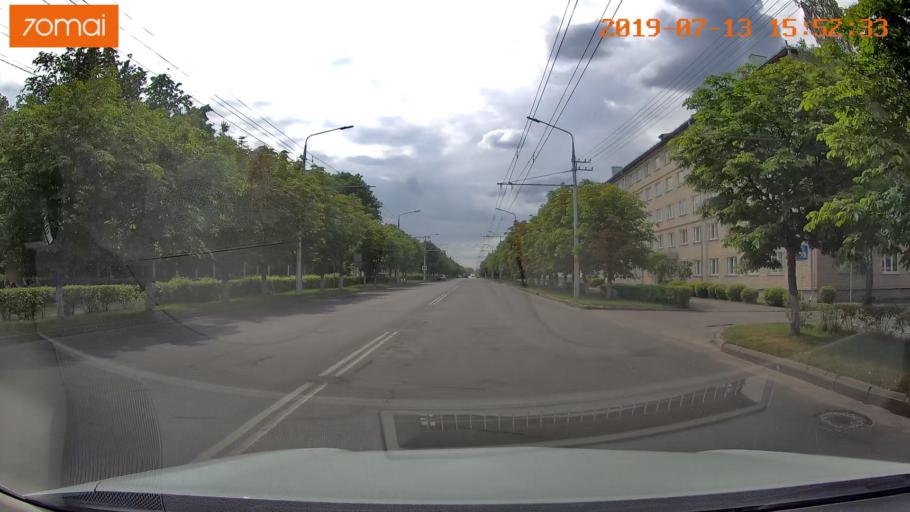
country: BY
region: Mogilev
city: Babruysk
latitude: 53.1392
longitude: 29.2143
